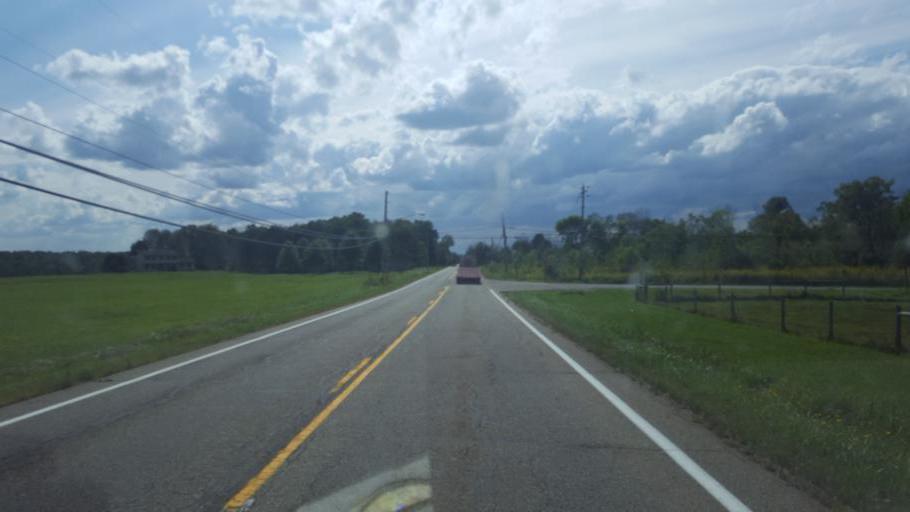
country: US
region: Ohio
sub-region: Portage County
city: Ravenna
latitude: 41.2091
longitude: -81.1824
